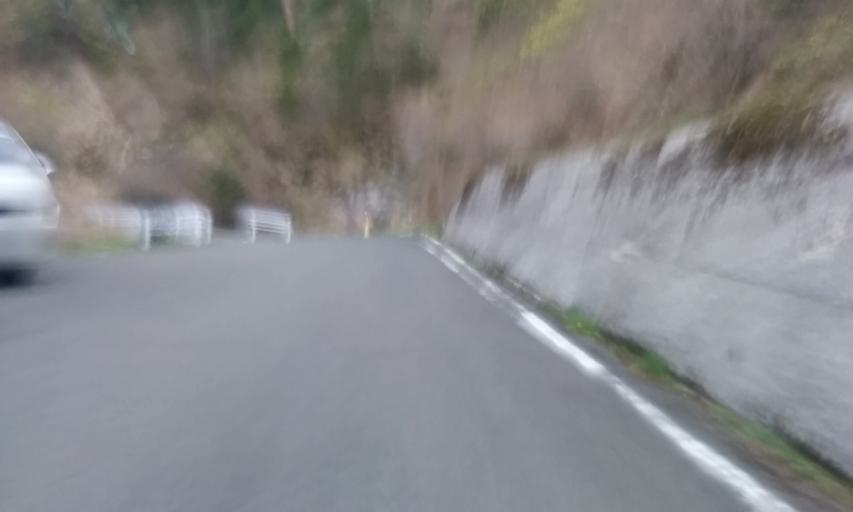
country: JP
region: Ehime
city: Saijo
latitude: 33.7862
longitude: 133.2453
